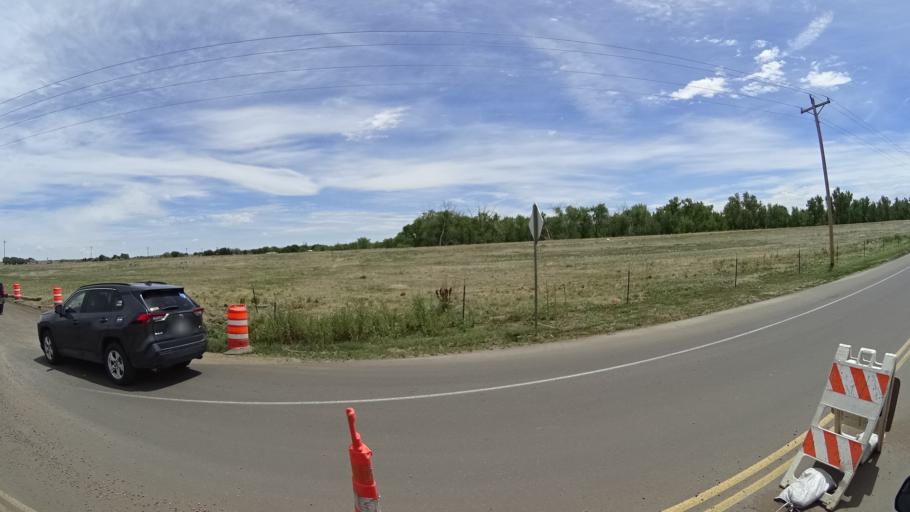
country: US
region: Colorado
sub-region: El Paso County
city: Fountain
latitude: 38.7071
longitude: -104.6737
